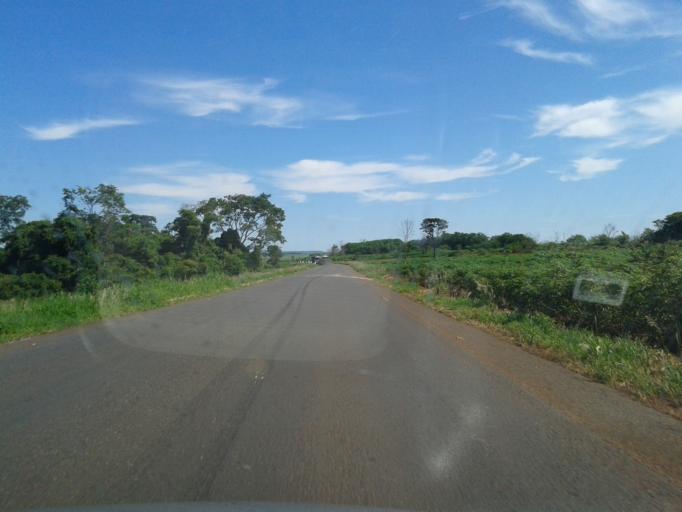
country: BR
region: Goias
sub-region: Bela Vista De Goias
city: Bela Vista de Goias
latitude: -17.1851
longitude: -48.7163
